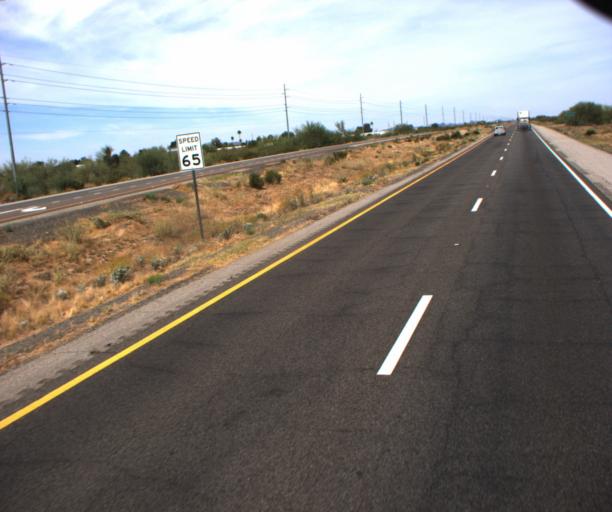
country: US
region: Arizona
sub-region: Maricopa County
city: Sun City West
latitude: 33.7854
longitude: -112.5381
